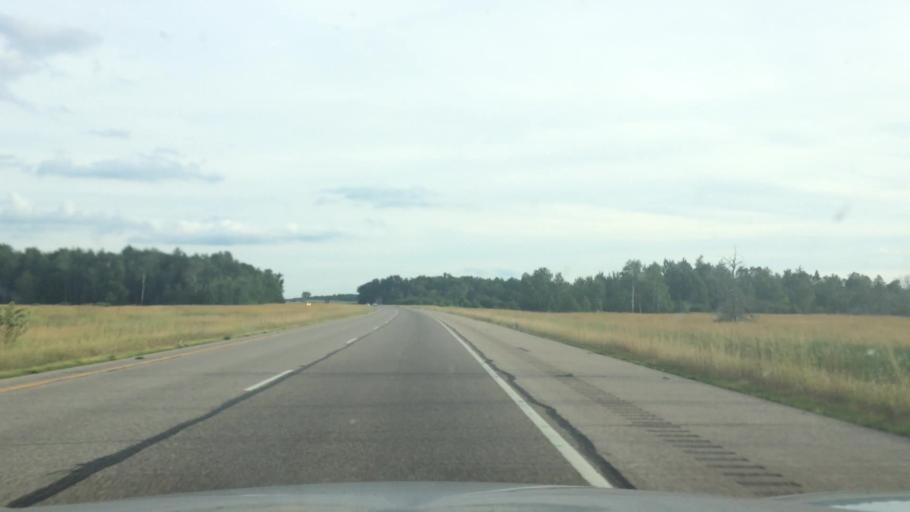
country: US
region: Wisconsin
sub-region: Waushara County
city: Wautoma
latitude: 44.1723
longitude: -89.5319
